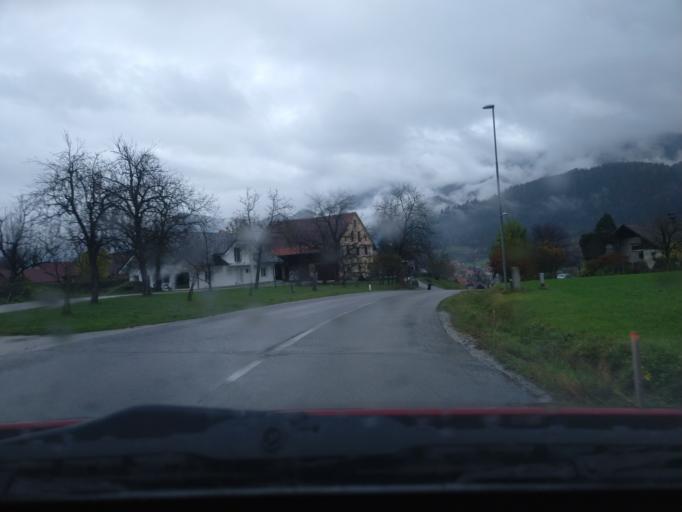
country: SI
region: Ljubno
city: Ljubno ob Savinji
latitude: 46.3267
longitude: 14.8481
